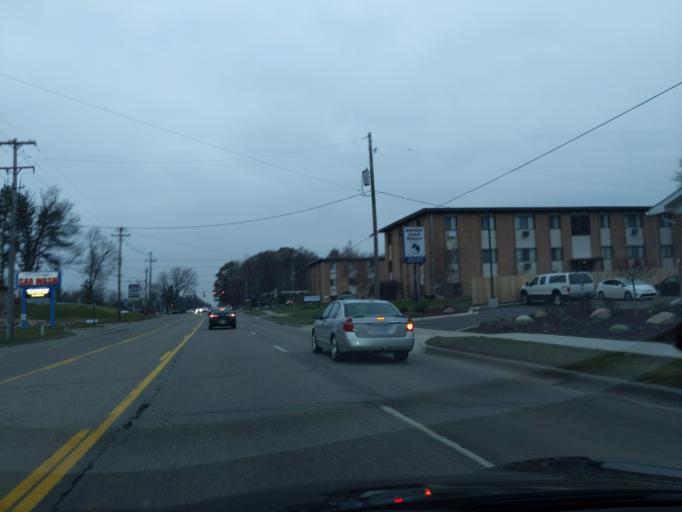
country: US
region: Michigan
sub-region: Ingham County
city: Edgemont Park
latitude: 42.7322
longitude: -84.6029
